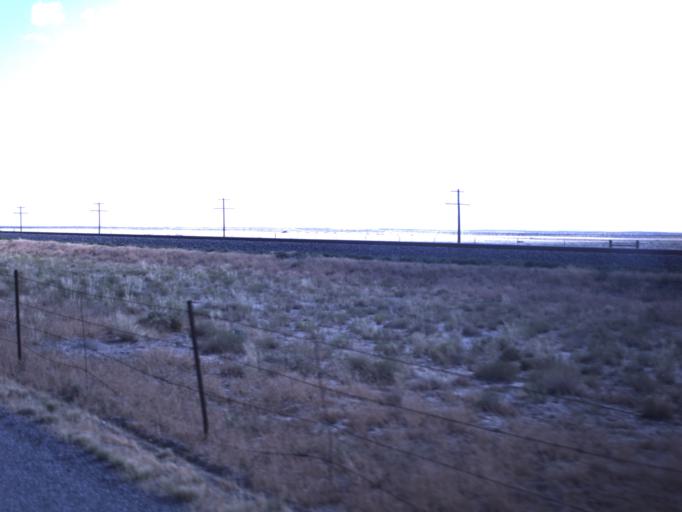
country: US
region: Utah
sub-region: Millard County
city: Delta
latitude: 38.9217
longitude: -112.8116
